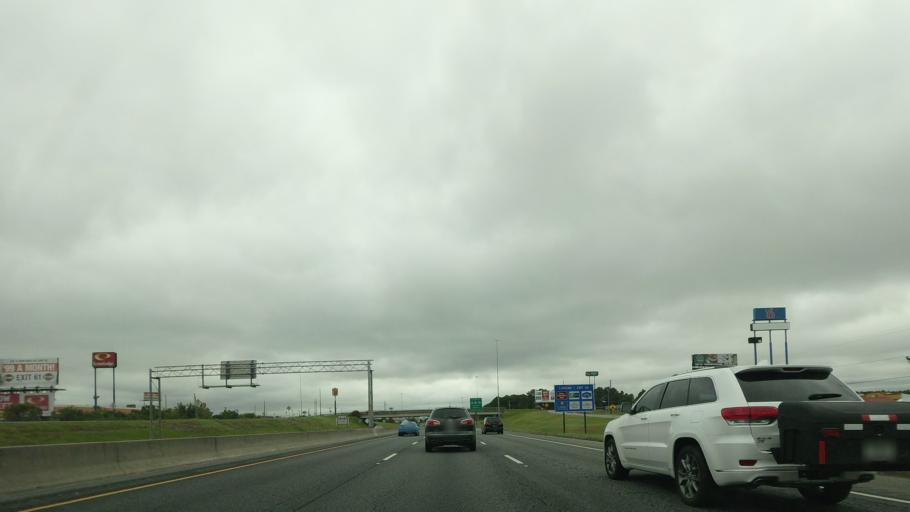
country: US
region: Georgia
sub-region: Tift County
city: Tifton
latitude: 31.4597
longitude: -83.5304
